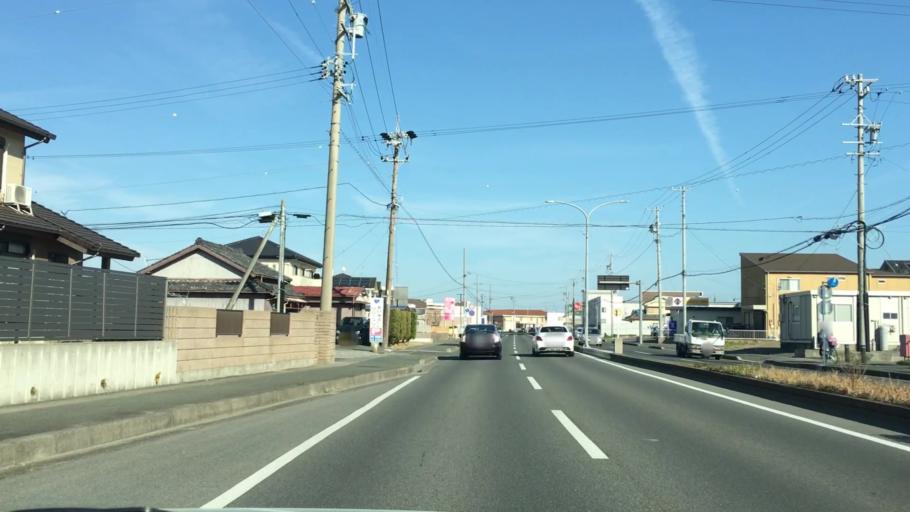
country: JP
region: Shizuoka
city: Hamamatsu
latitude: 34.6958
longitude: 137.6375
